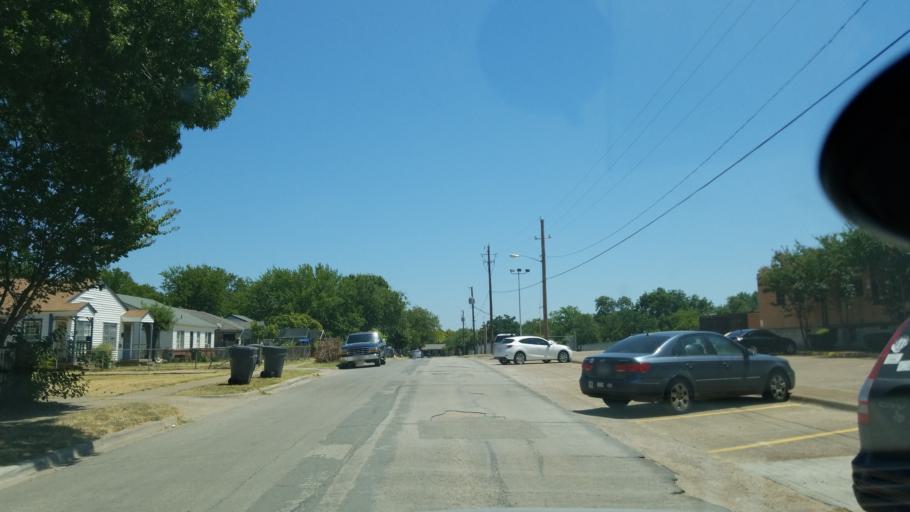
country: US
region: Texas
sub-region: Dallas County
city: Cockrell Hill
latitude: 32.7331
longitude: -96.8872
